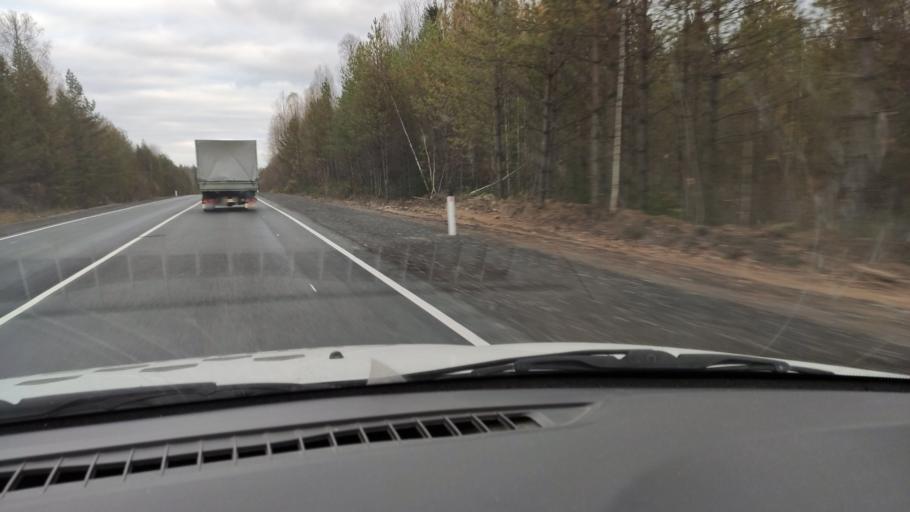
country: RU
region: Kirov
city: Chernaya Kholunitsa
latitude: 58.8730
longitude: 51.5147
